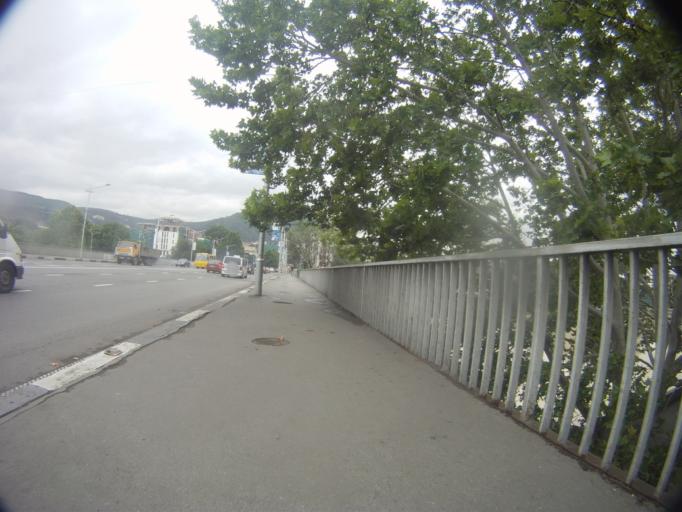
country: GE
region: T'bilisi
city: Tbilisi
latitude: 41.6970
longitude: 44.8086
